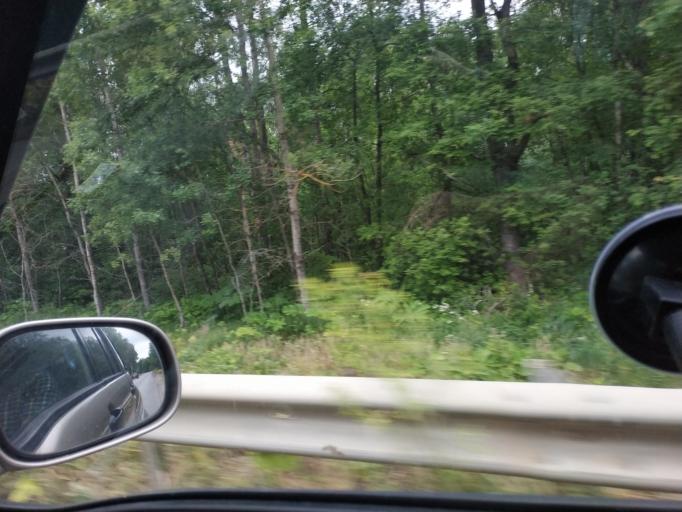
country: RU
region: Moskovskaya
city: Krasnoarmeysk
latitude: 56.0779
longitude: 38.2434
